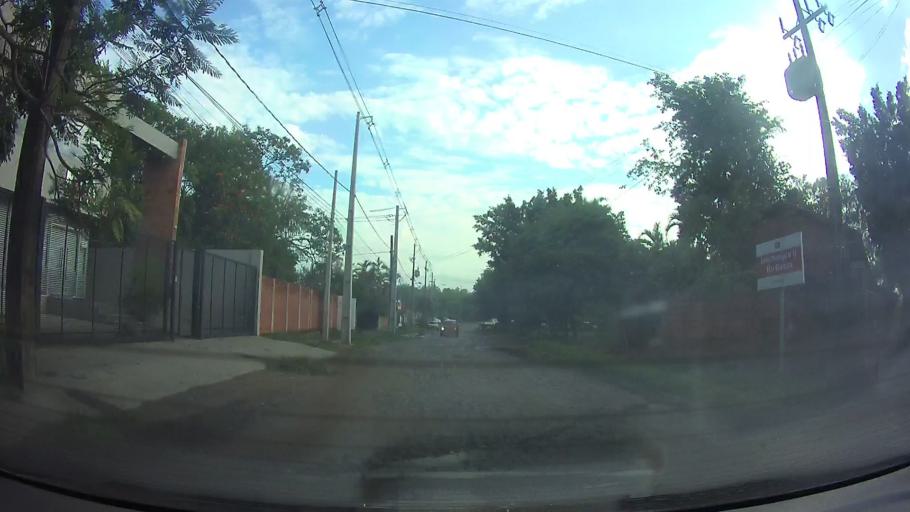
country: PY
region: Central
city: Fernando de la Mora
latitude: -25.2623
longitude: -57.5488
